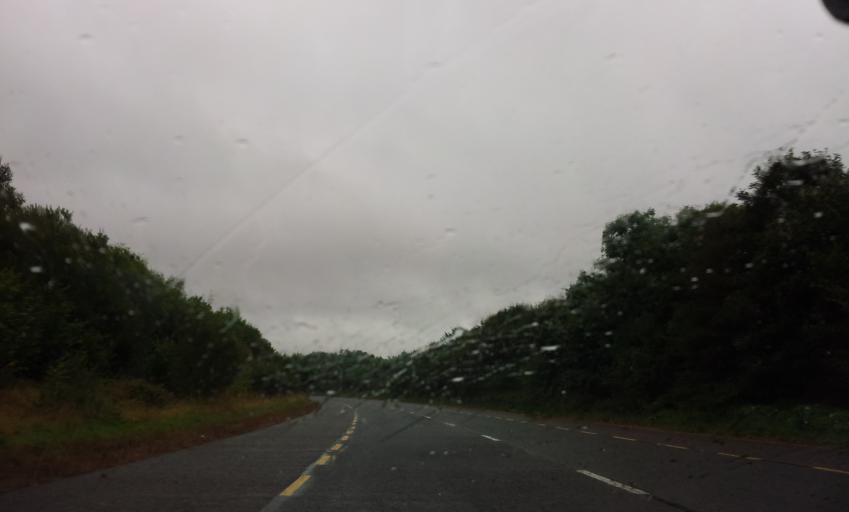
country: IE
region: Munster
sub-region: County Cork
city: Blarney
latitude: 51.9506
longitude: -8.5708
